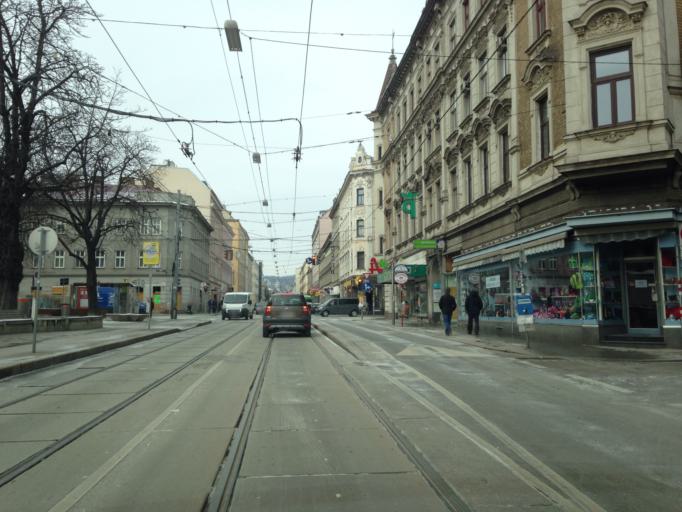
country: AT
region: Vienna
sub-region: Wien Stadt
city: Vienna
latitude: 48.2115
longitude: 16.3199
